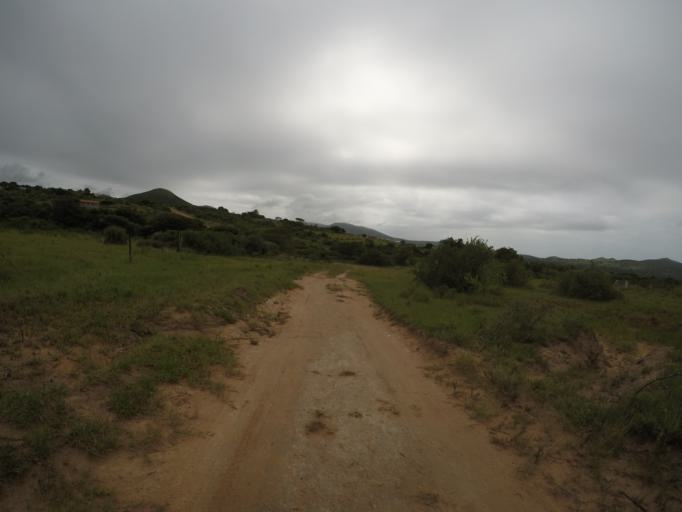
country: ZA
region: KwaZulu-Natal
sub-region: uThungulu District Municipality
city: Empangeni
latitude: -28.6116
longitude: 31.8441
